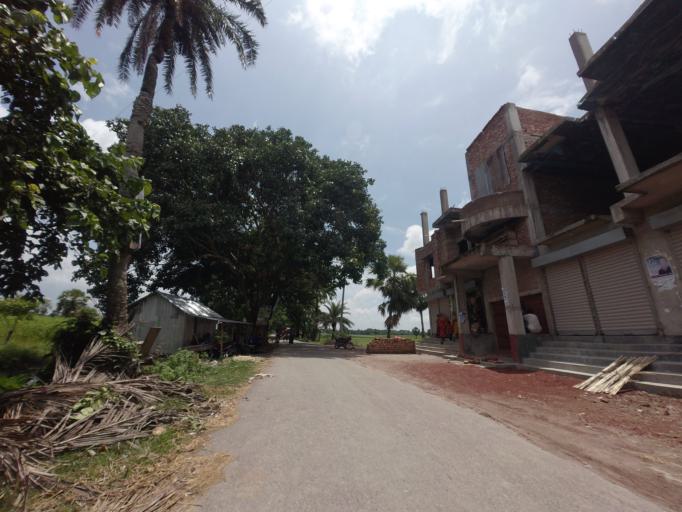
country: BD
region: Khulna
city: Kalia
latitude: 23.0433
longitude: 89.6524
